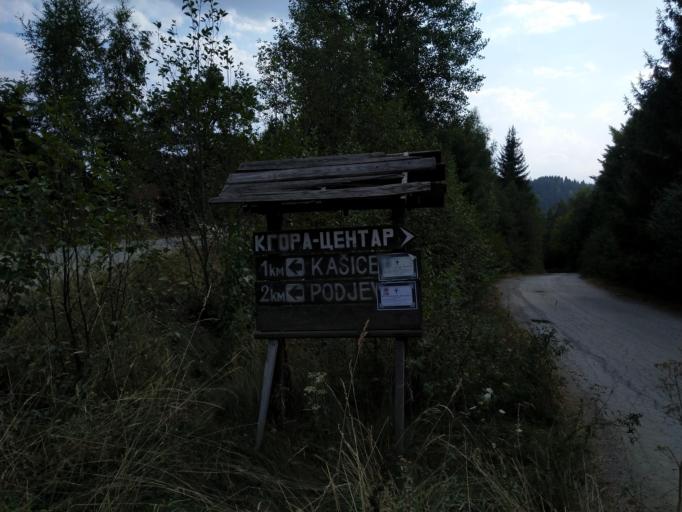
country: RS
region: Central Serbia
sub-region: Zlatiborski Okrug
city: Prijepolje
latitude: 43.2958
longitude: 19.5861
